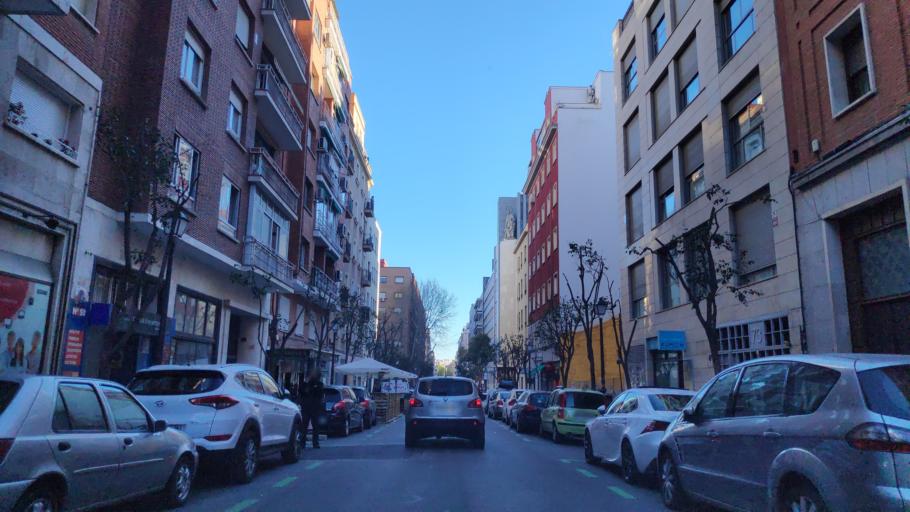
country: ES
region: Madrid
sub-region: Provincia de Madrid
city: Chamberi
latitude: 40.4385
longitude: -3.7153
